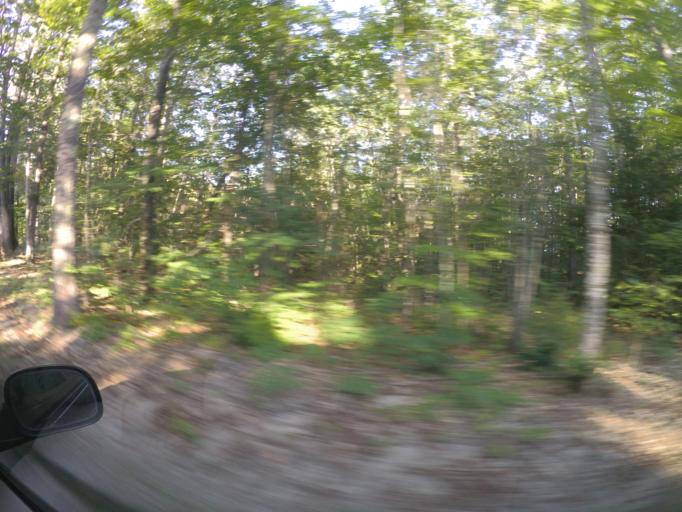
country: US
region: Maine
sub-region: Cumberland County
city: Raymond
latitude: 43.8879
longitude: -70.4179
